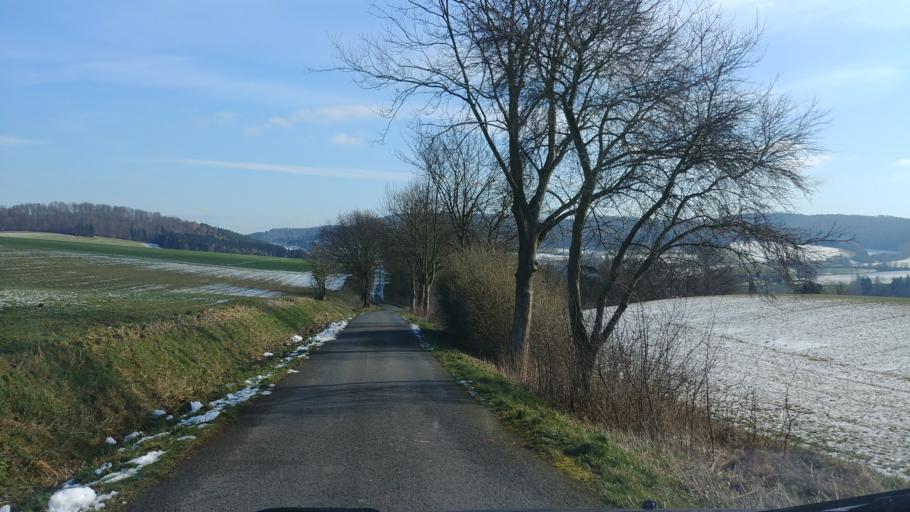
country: DE
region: Lower Saxony
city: Uslar
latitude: 51.6583
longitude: 9.6668
